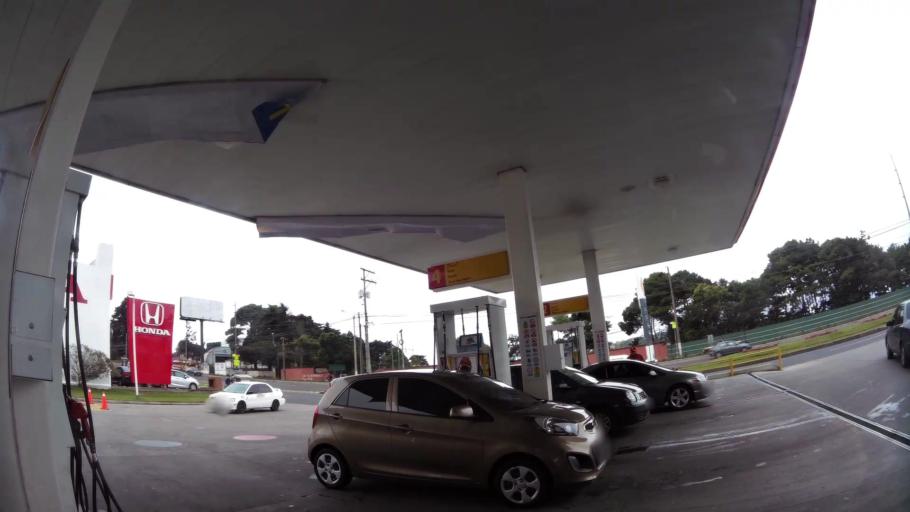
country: GT
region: Guatemala
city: San Jose Pinula
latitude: 14.5494
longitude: -90.4544
